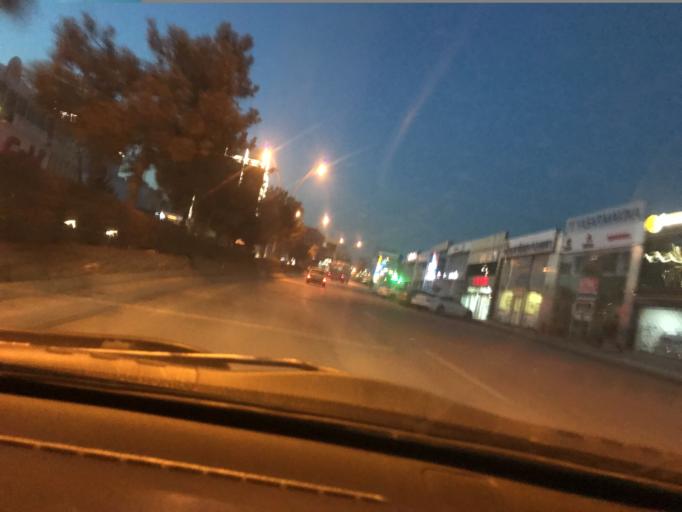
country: TR
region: Ankara
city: Batikent
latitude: 39.9672
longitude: 32.7465
